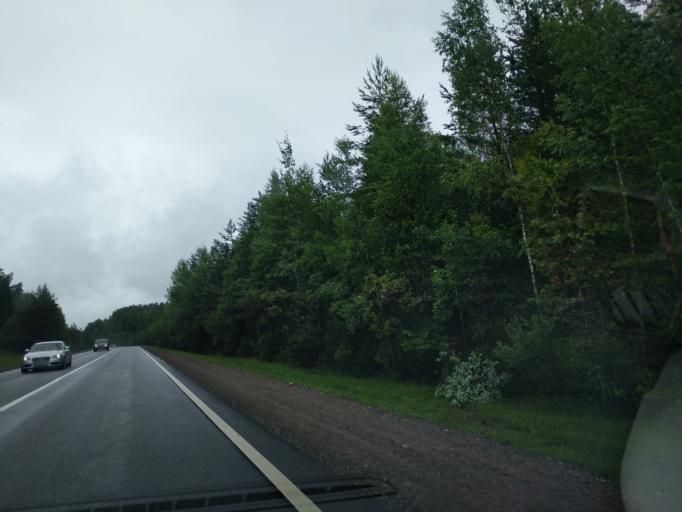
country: BY
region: Minsk
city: Syomkava
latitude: 54.2159
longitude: 27.4966
